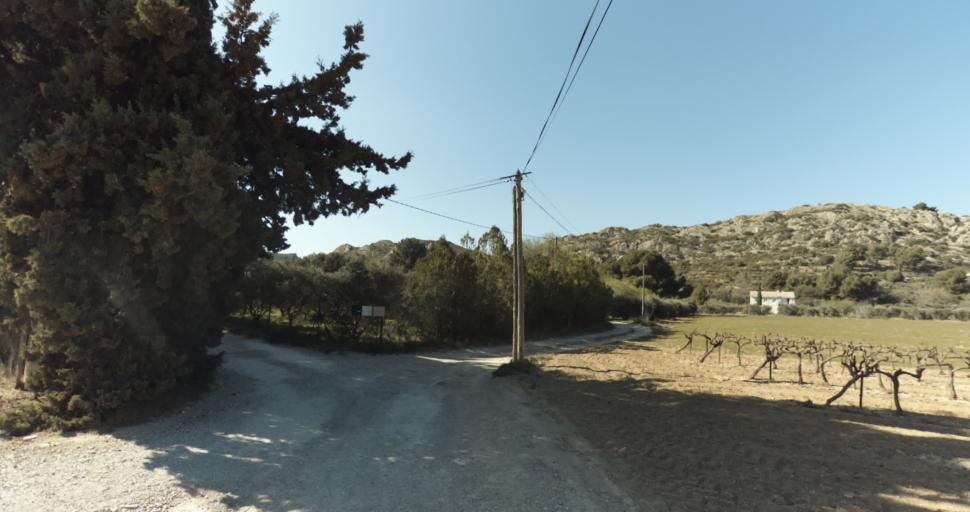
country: FR
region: Provence-Alpes-Cote d'Azur
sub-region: Departement des Bouches-du-Rhone
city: Pelissanne
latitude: 43.6401
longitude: 5.1412
